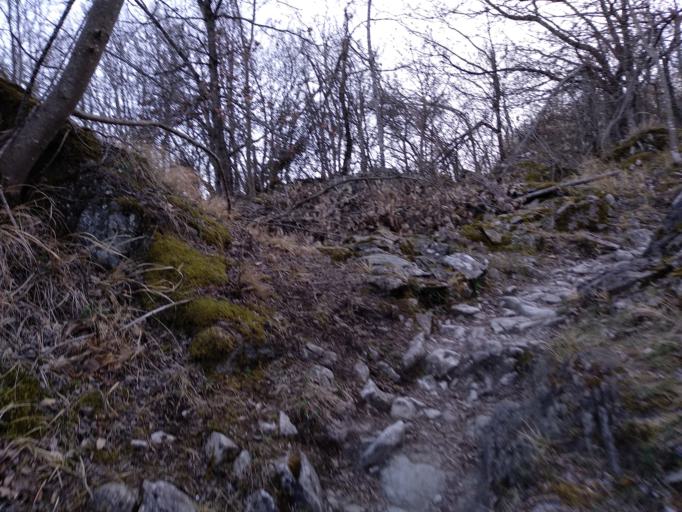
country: IT
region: Emilia-Romagna
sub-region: Provincia di Reggio Emilia
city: Castelnovo ne'Monti
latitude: 44.4231
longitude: 10.4202
